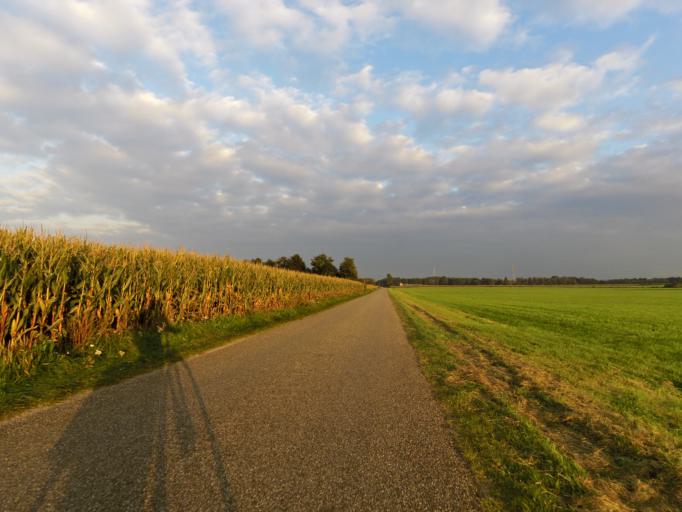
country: NL
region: Gelderland
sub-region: Gemeente Doesburg
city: Doesburg
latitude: 51.9420
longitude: 6.1711
